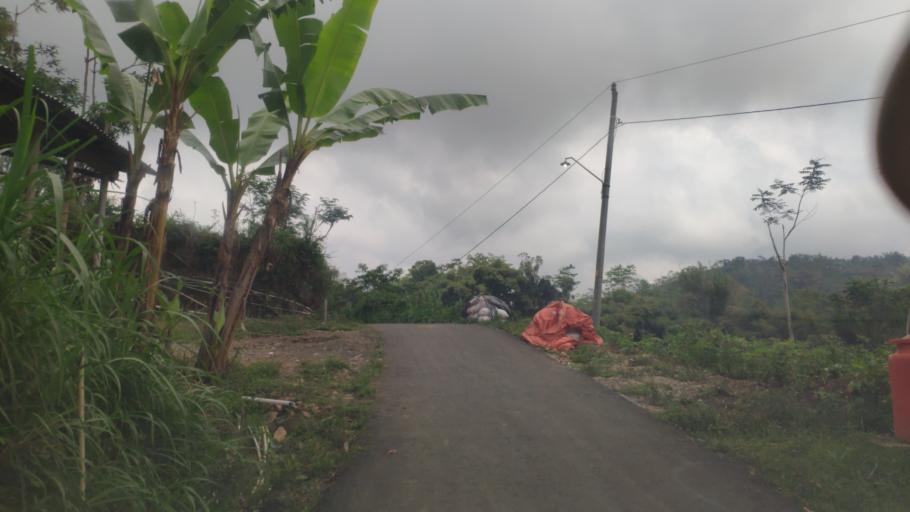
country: ID
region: Central Java
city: Wonosobo
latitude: -7.2636
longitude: 109.7245
